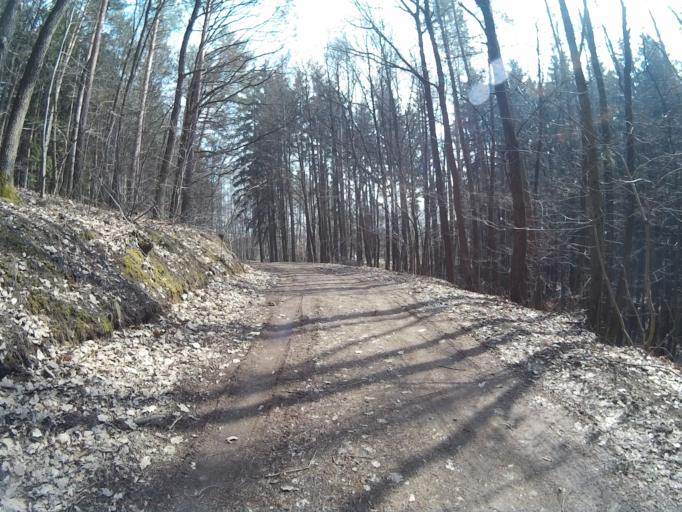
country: CZ
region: South Moravian
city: Pozorice
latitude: 49.2217
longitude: 16.7928
